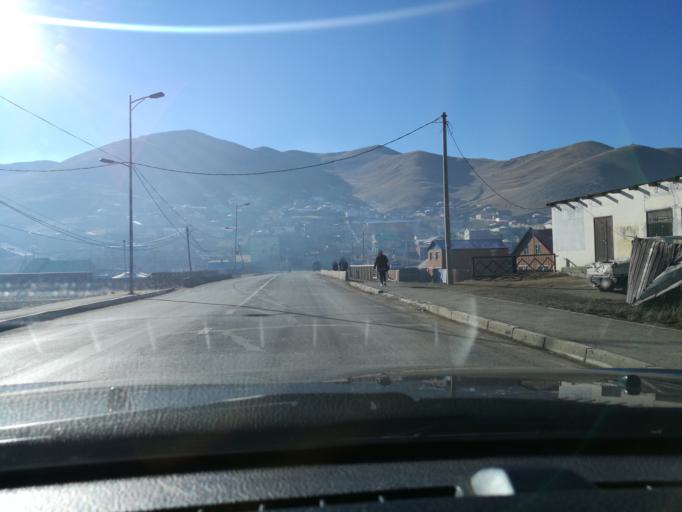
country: MN
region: Ulaanbaatar
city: Ulaanbaatar
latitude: 47.9793
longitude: 106.9387
